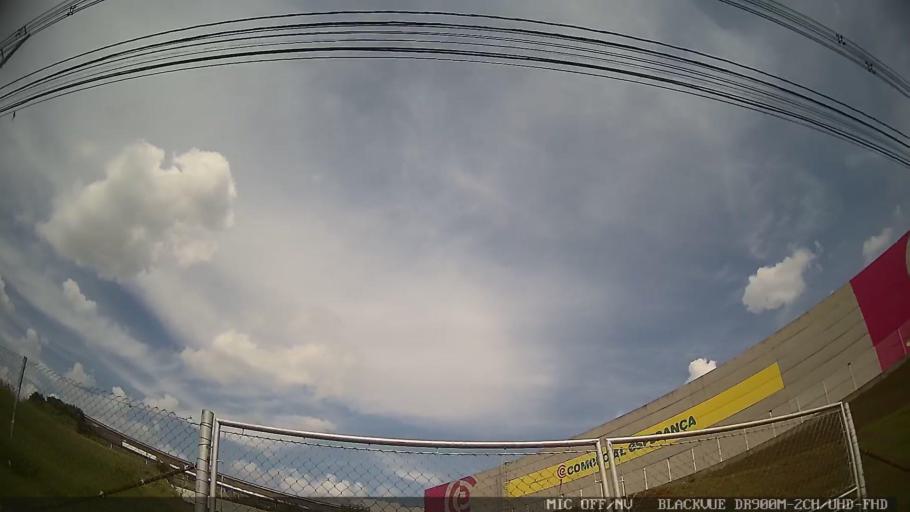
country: BR
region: Sao Paulo
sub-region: Braganca Paulista
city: Braganca Paulista
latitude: -22.9474
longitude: -46.5284
